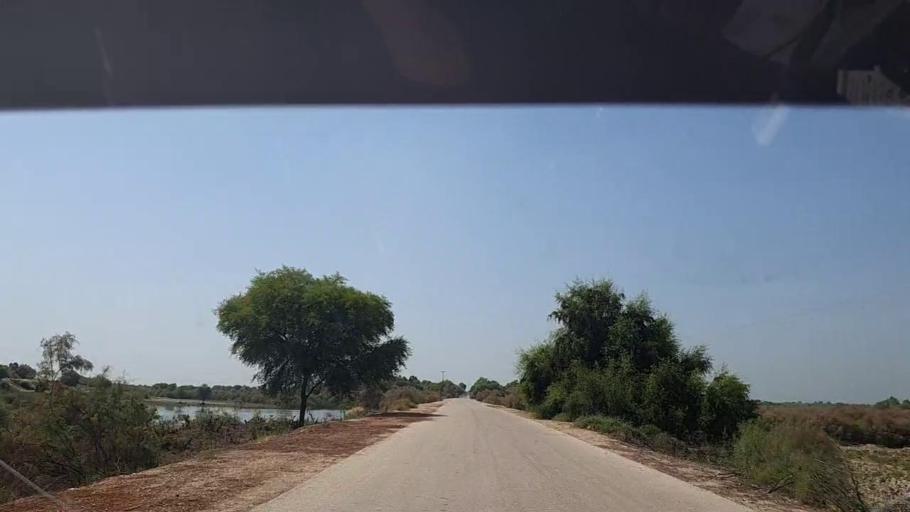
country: PK
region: Sindh
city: Ghauspur
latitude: 28.1545
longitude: 69.1578
